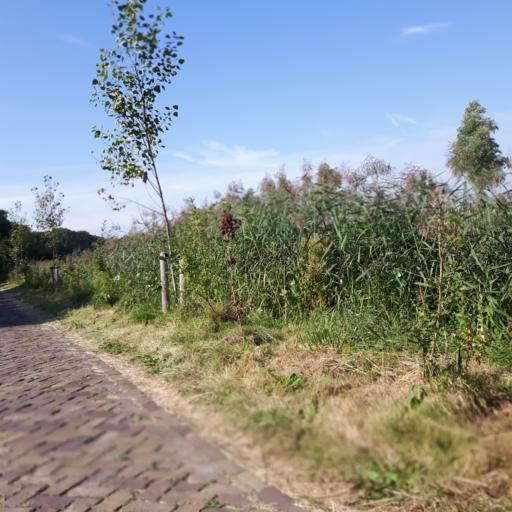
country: NL
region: Zeeland
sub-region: Gemeente Middelburg
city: Middelburg
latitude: 51.4561
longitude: 3.6463
